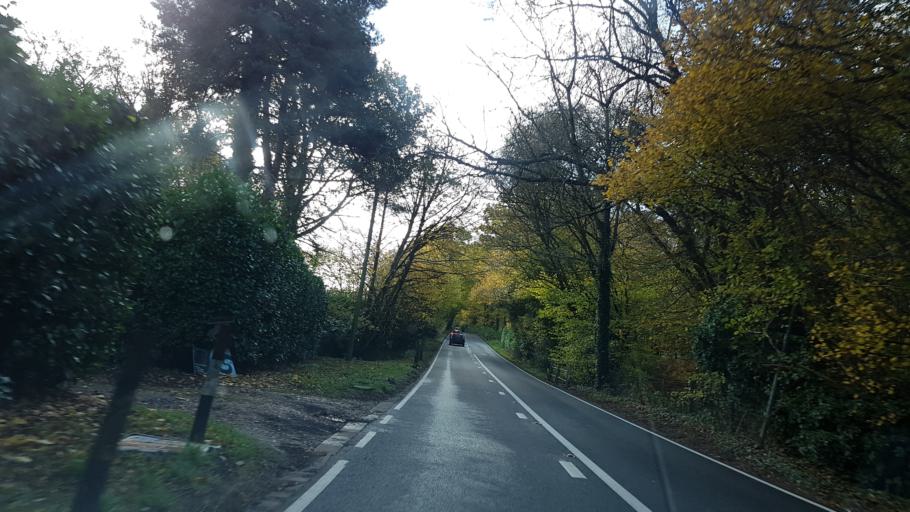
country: GB
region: England
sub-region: Surrey
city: Haslemere
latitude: 51.1231
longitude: -0.6736
